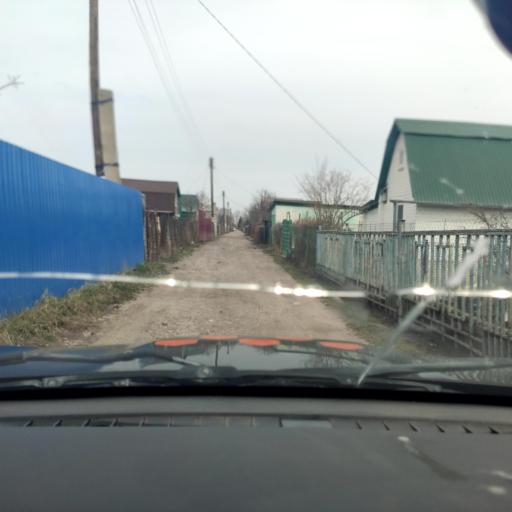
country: RU
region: Samara
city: Tol'yatti
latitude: 53.6001
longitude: 49.2456
